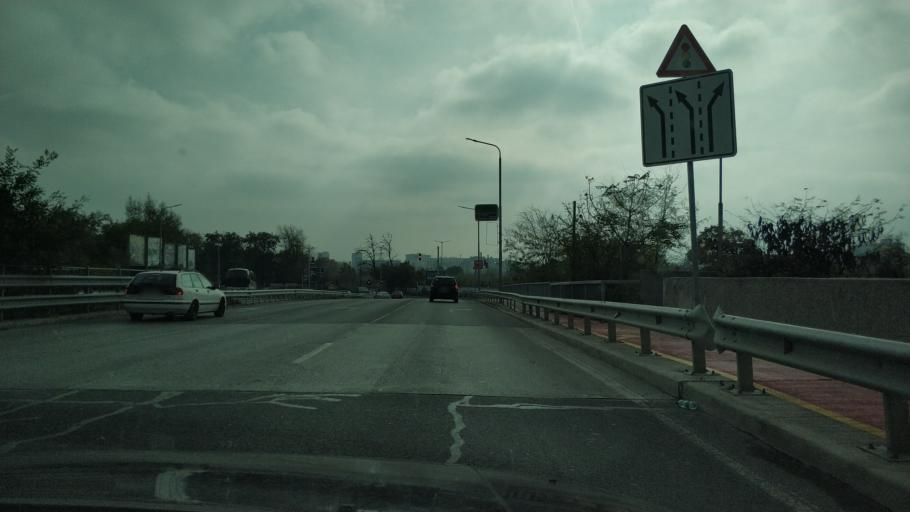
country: BG
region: Plovdiv
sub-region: Obshtina Plovdiv
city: Plovdiv
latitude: 42.1540
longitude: 24.7658
